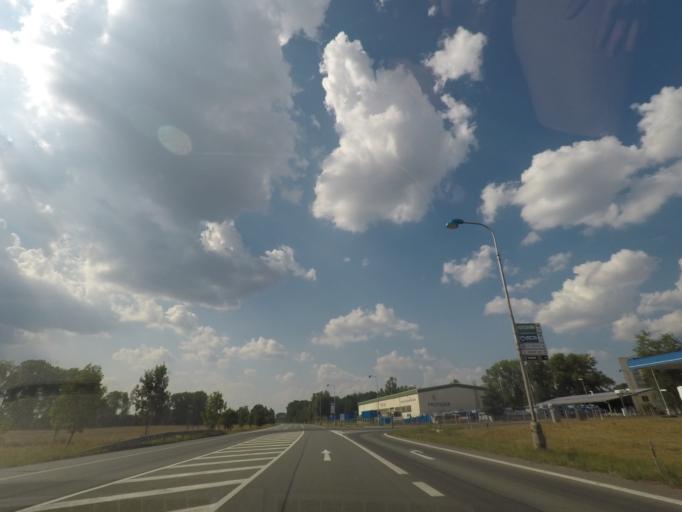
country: CZ
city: Tyniste nad Orlici
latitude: 50.1574
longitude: 16.0638
